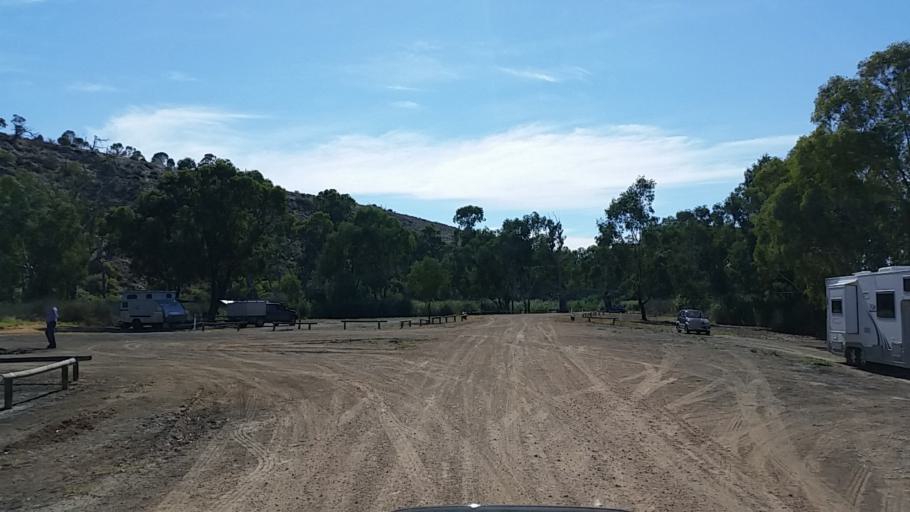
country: AU
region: South Australia
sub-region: Mid Murray
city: Mannum
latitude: -34.7006
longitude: 139.5758
